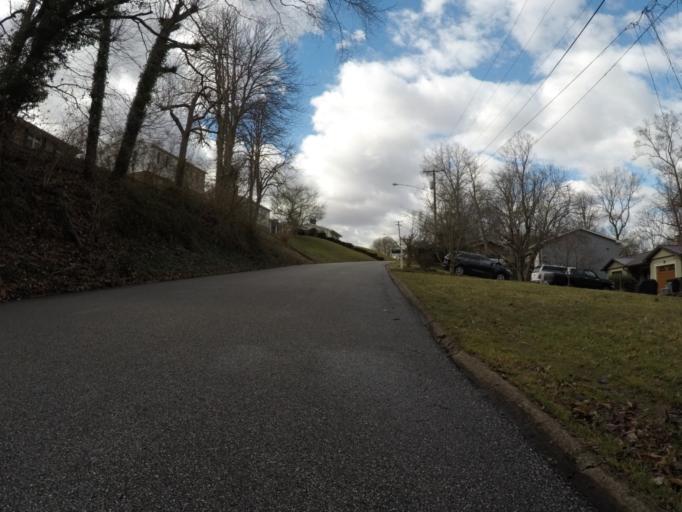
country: US
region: West Virginia
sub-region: Cabell County
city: Huntington
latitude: 38.4101
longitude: -82.3872
